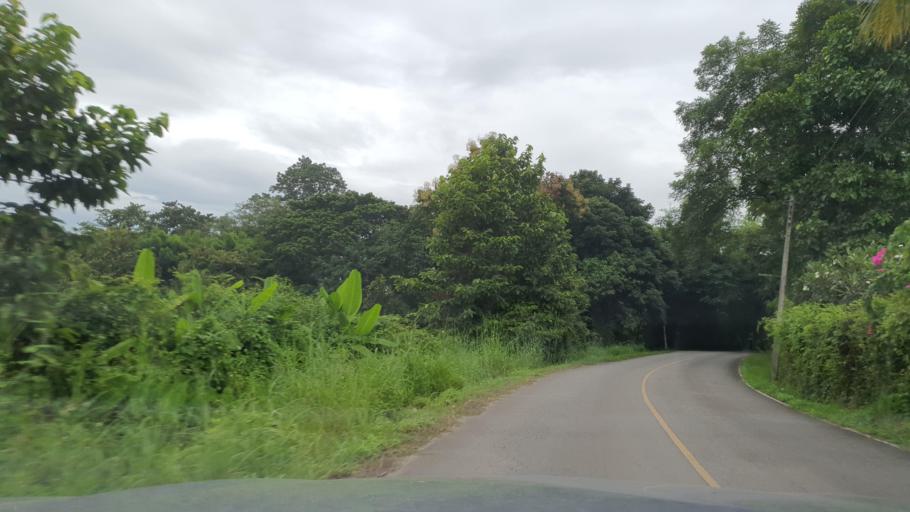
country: TH
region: Chiang Mai
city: San Sai
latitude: 18.9295
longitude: 98.9303
